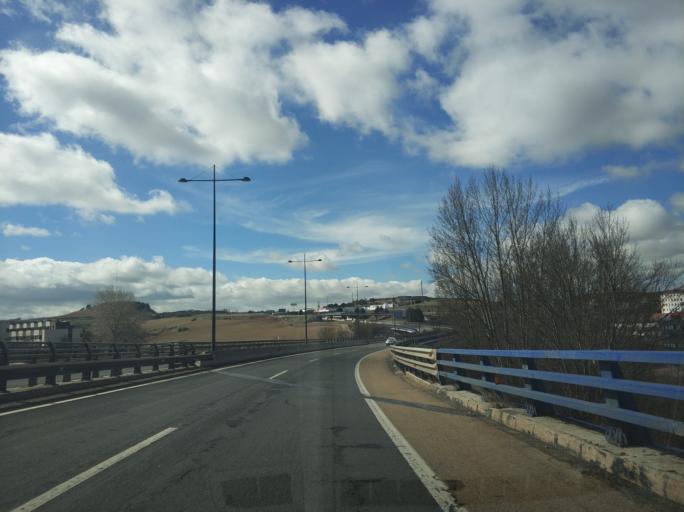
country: ES
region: Castille and Leon
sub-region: Provincia de Burgos
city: Burgos
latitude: 42.3269
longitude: -3.6972
